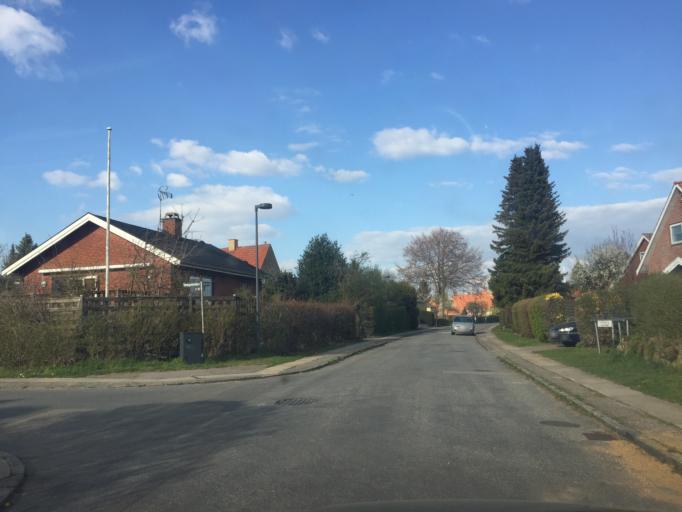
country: DK
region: Capital Region
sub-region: Herlev Kommune
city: Herlev
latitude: 55.7068
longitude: 12.4606
